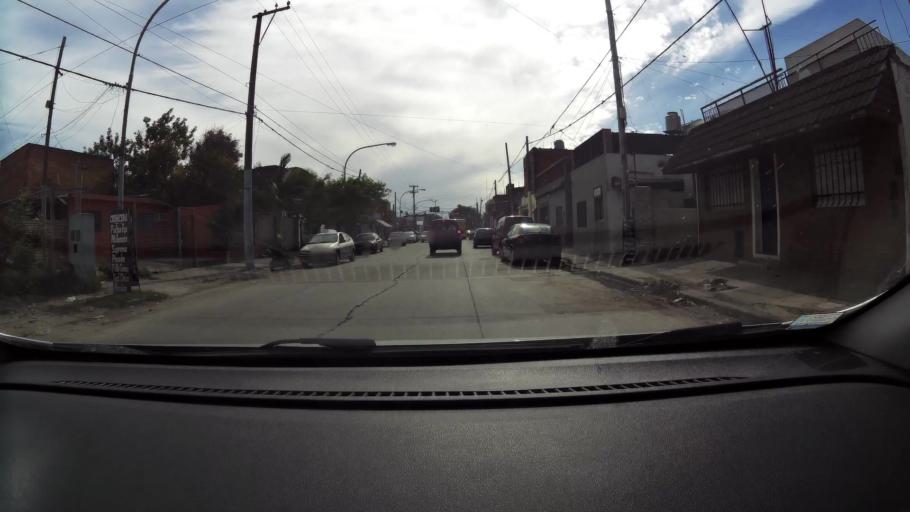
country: AR
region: Santa Fe
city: Granadero Baigorria
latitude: -32.9160
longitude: -60.7127
